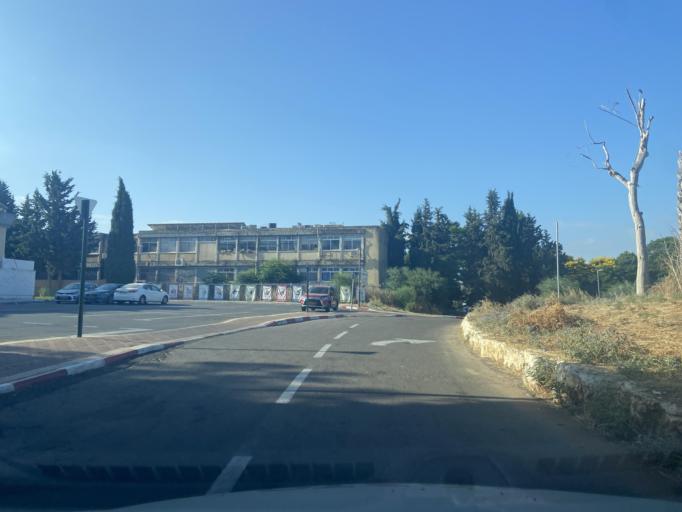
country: IL
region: Central District
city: Yehud
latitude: 32.0407
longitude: 34.8920
